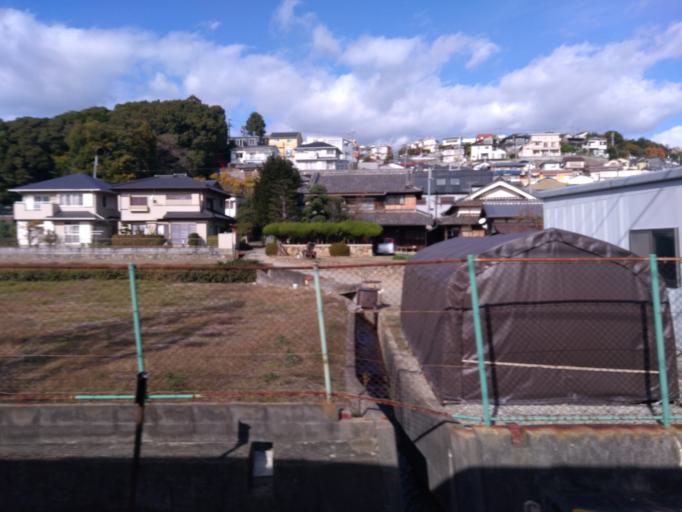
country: JP
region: Hyogo
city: Takarazuka
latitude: 34.8207
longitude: 135.3791
